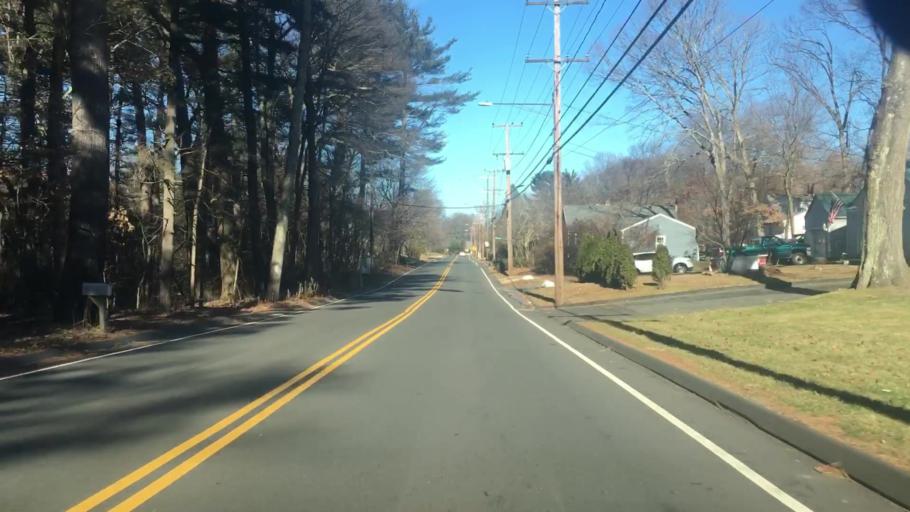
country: US
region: Connecticut
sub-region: Hartford County
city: Plainville
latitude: 41.6646
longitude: -72.9021
